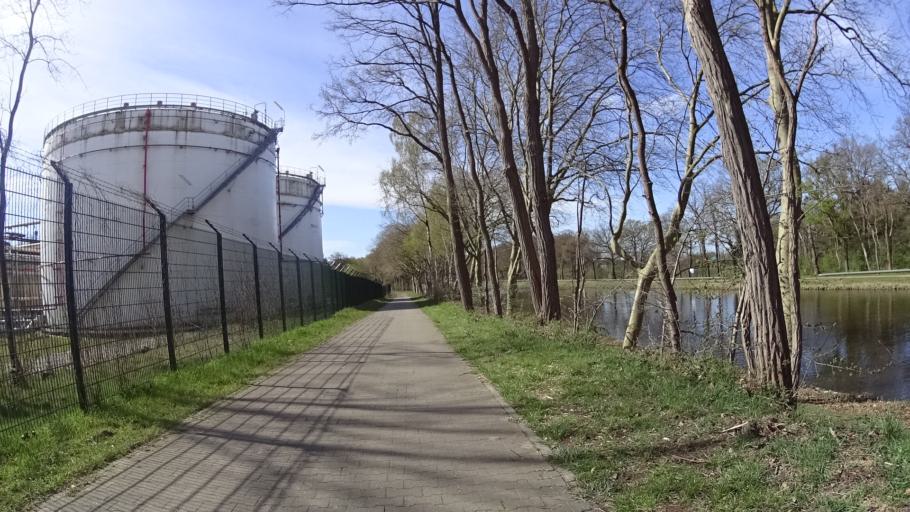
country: DE
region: Lower Saxony
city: Lingen
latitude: 52.5583
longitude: 7.2990
